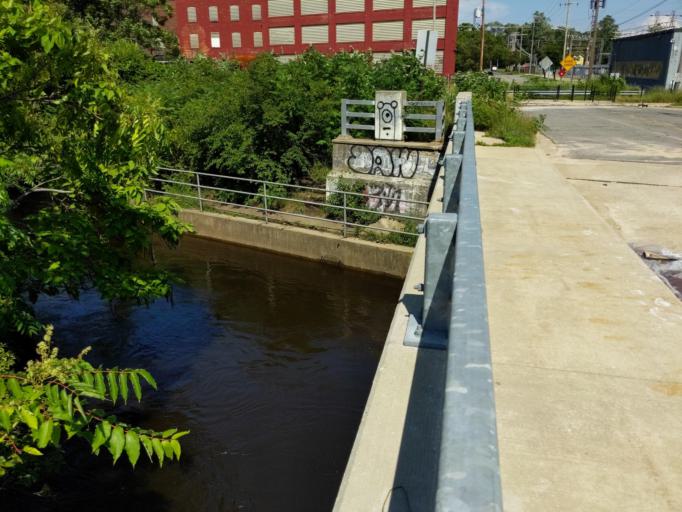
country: US
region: Michigan
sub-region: Jackson County
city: Jackson
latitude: 42.2524
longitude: -84.4080
